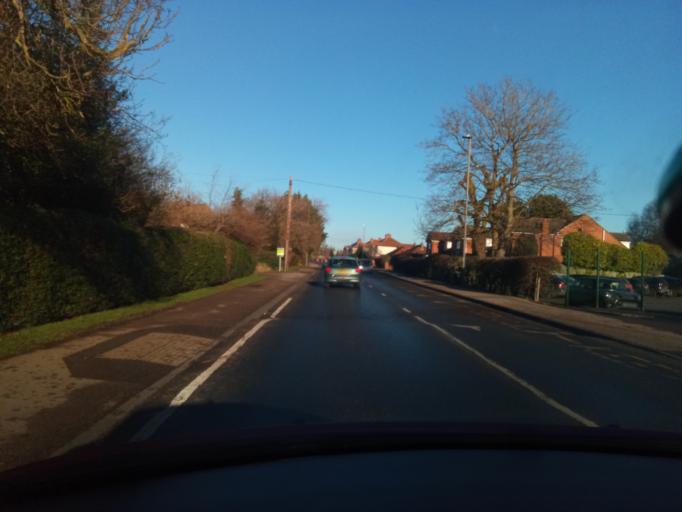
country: GB
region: England
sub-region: North Yorkshire
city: Thirsk
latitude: 54.2238
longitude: -1.3487
